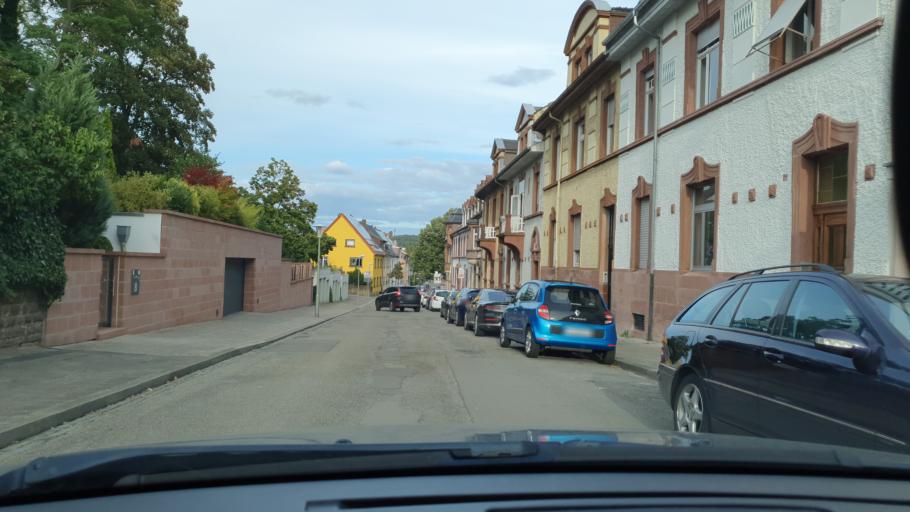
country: DE
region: Rheinland-Pfalz
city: Kaiserslautern
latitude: 49.4505
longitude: 7.7734
